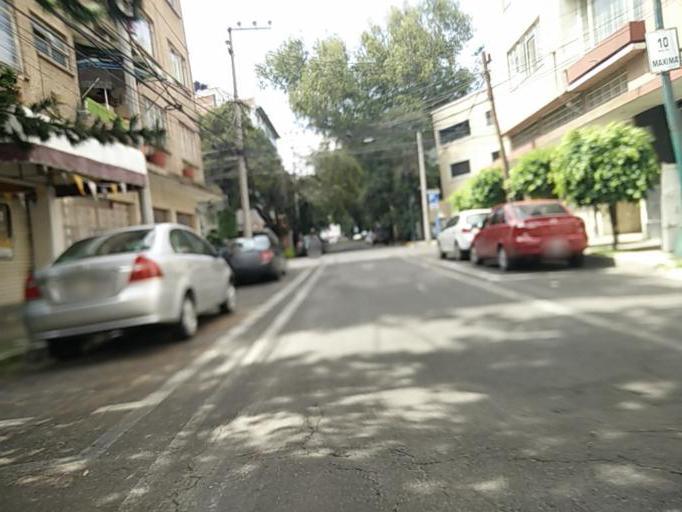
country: MX
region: Mexico City
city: Miguel Hidalgo
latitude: 19.4334
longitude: -99.1767
